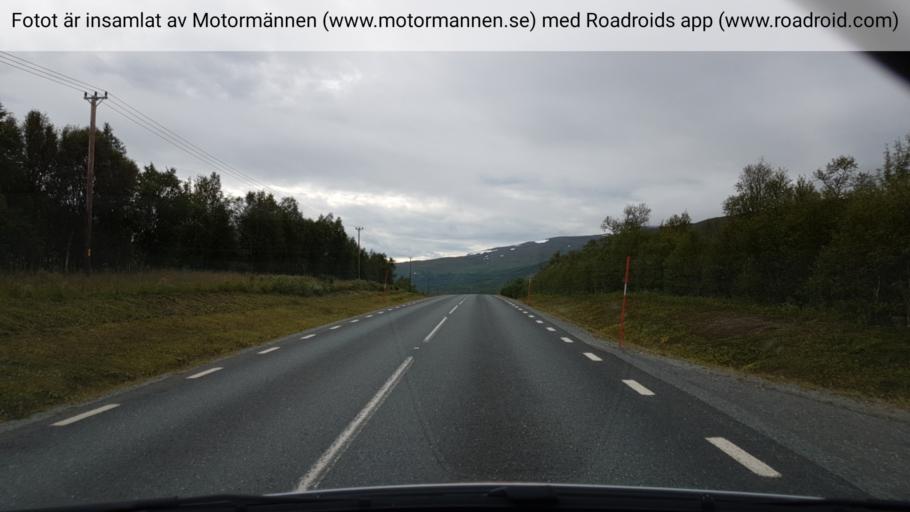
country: NO
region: Nordland
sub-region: Rana
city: Mo i Rana
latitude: 65.9189
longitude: 14.9993
